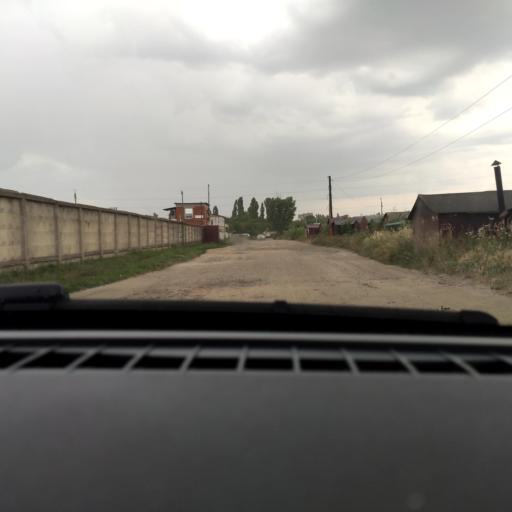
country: RU
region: Voronezj
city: Maslovka
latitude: 51.6408
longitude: 39.2806
